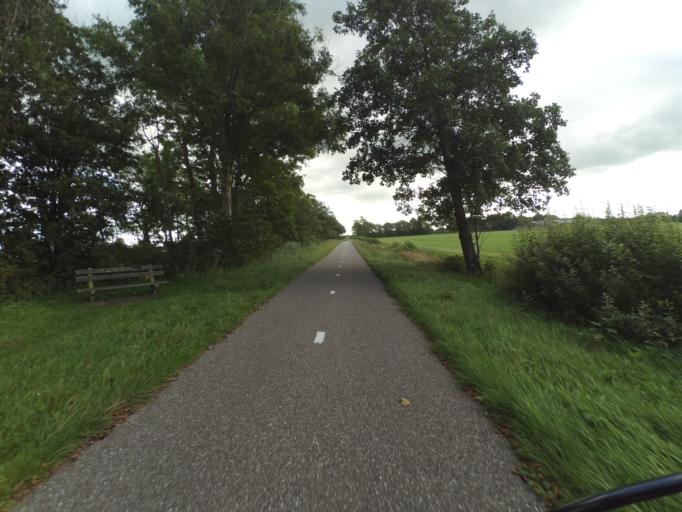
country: NL
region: Friesland
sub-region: Gemeente Tytsjerksteradiel
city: Hurdegaryp
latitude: 53.2065
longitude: 5.9572
